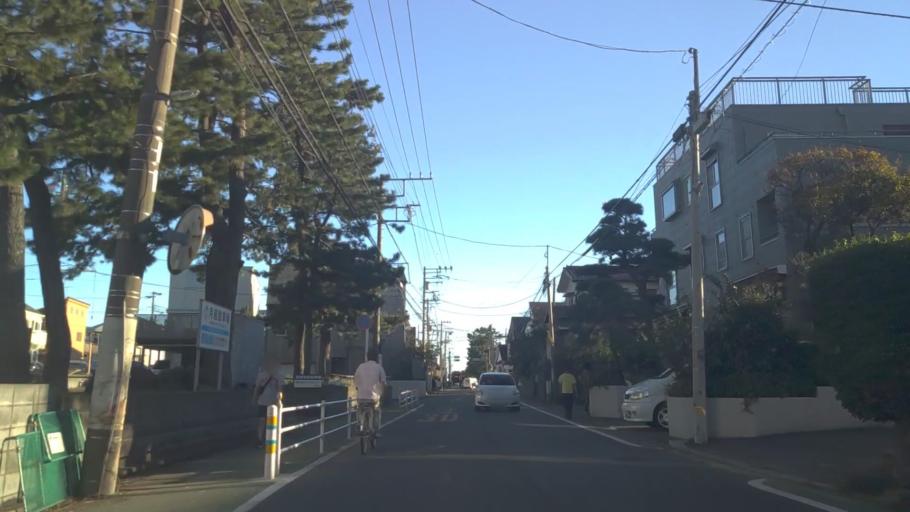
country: JP
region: Kanagawa
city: Chigasaki
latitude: 35.3220
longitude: 139.4154
